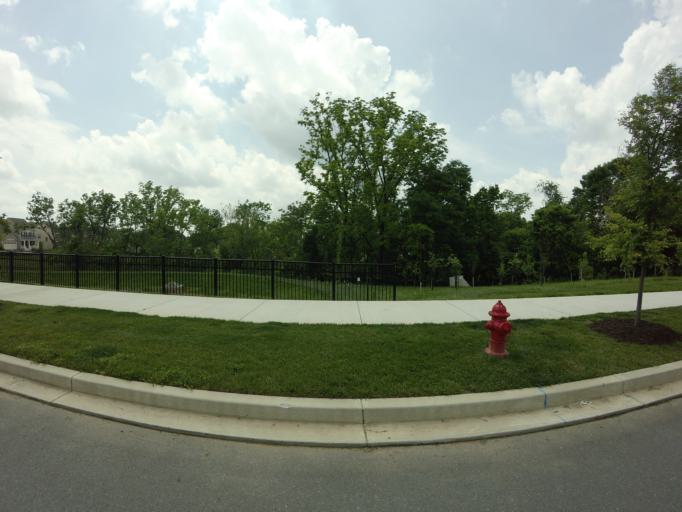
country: US
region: Maryland
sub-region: Frederick County
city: Brunswick
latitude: 39.3282
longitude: -77.6321
